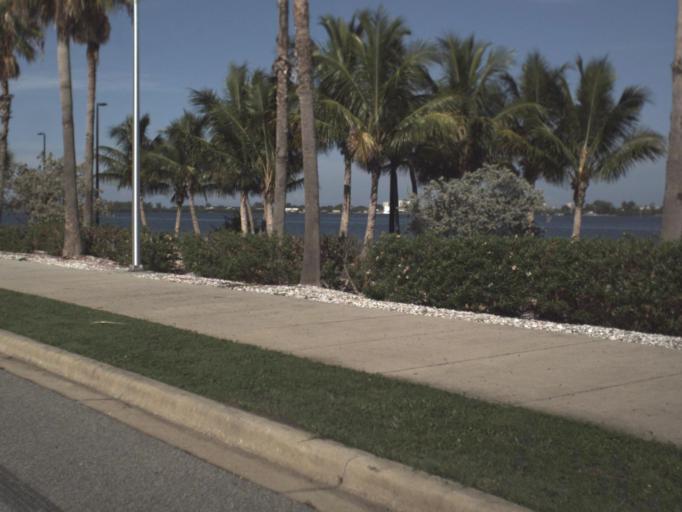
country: US
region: Florida
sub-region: Sarasota County
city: Siesta Key
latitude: 27.3271
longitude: -82.5613
